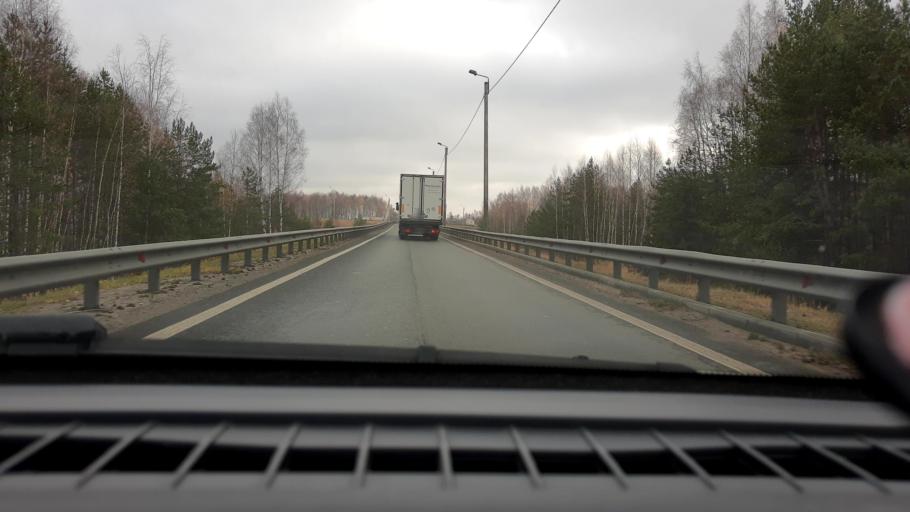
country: RU
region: Nizjnij Novgorod
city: Gorbatovka
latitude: 56.3049
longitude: 43.6830
